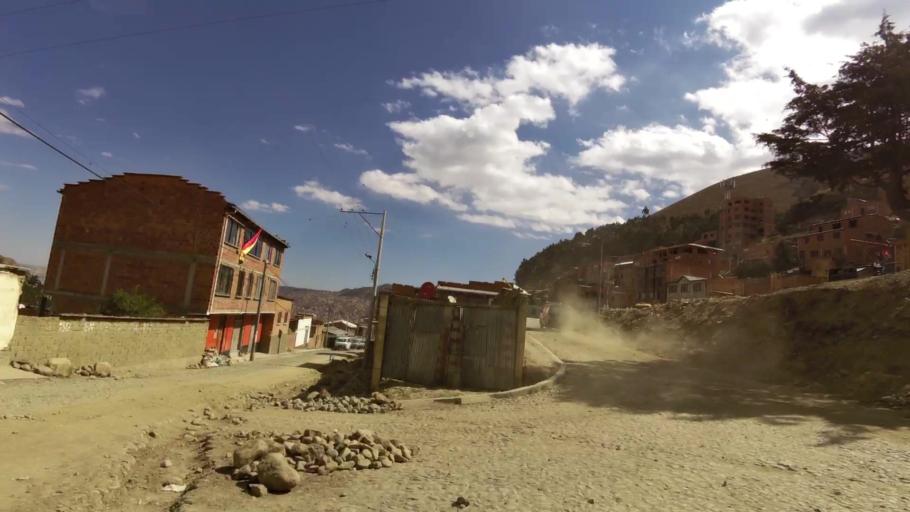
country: BO
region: La Paz
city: La Paz
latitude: -16.4621
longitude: -68.1061
